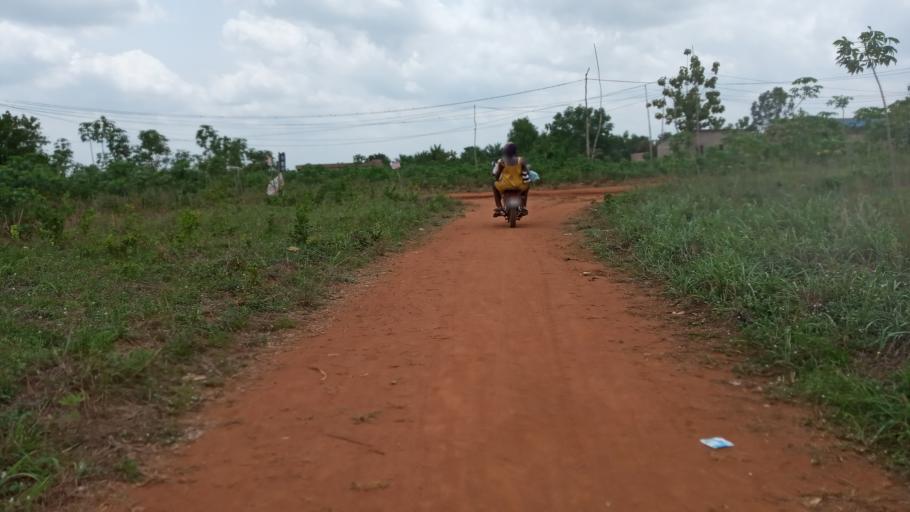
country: TG
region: Maritime
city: Tsevie
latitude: 6.2952
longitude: 1.1324
